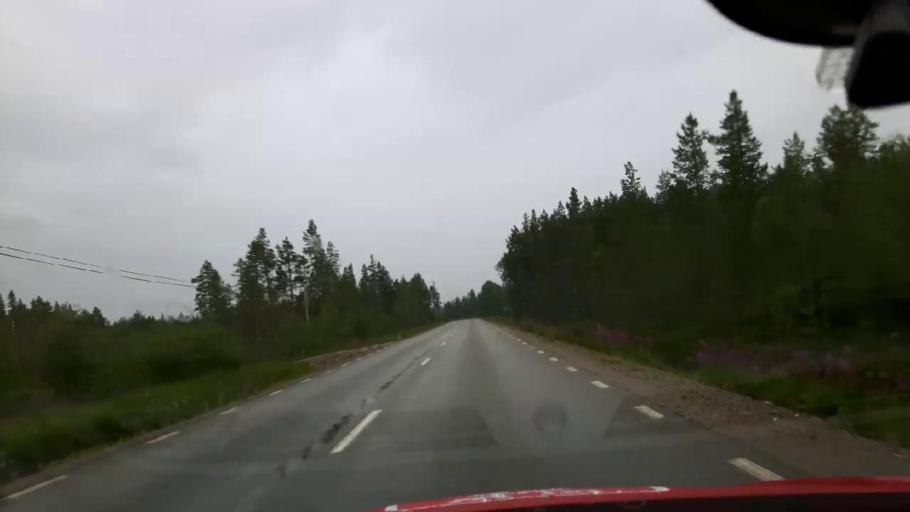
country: SE
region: Jaemtland
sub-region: OEstersunds Kommun
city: Brunflo
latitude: 62.7895
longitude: 15.0060
